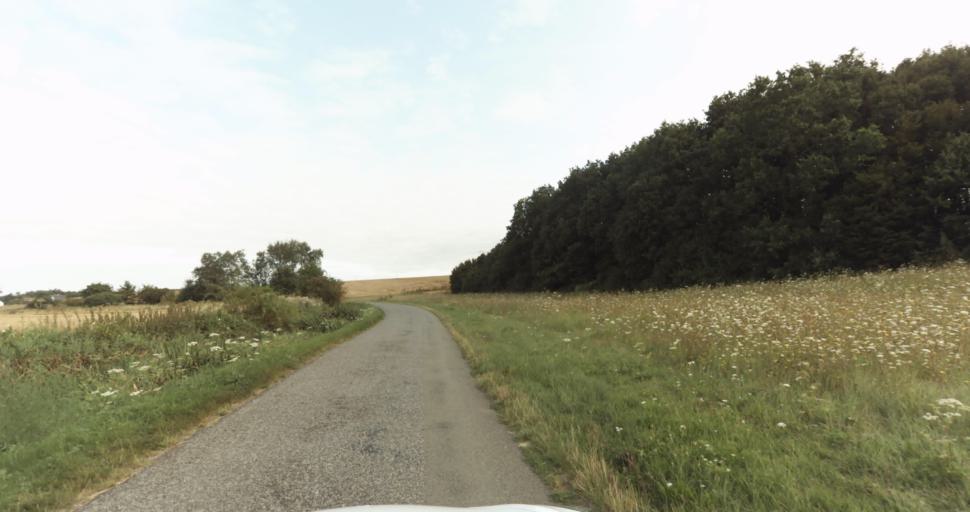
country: FR
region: Haute-Normandie
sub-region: Departement de l'Eure
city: Saint-Germain-sur-Avre
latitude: 48.8140
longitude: 1.2777
